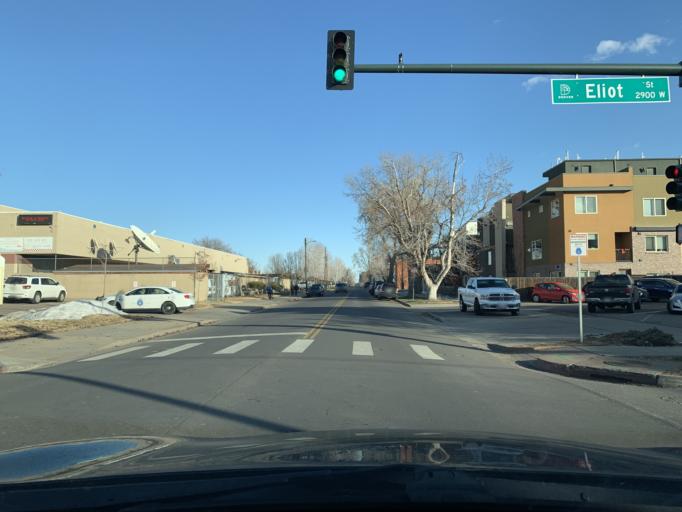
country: US
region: Colorado
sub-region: Jefferson County
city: Edgewater
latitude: 39.7548
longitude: -105.0237
